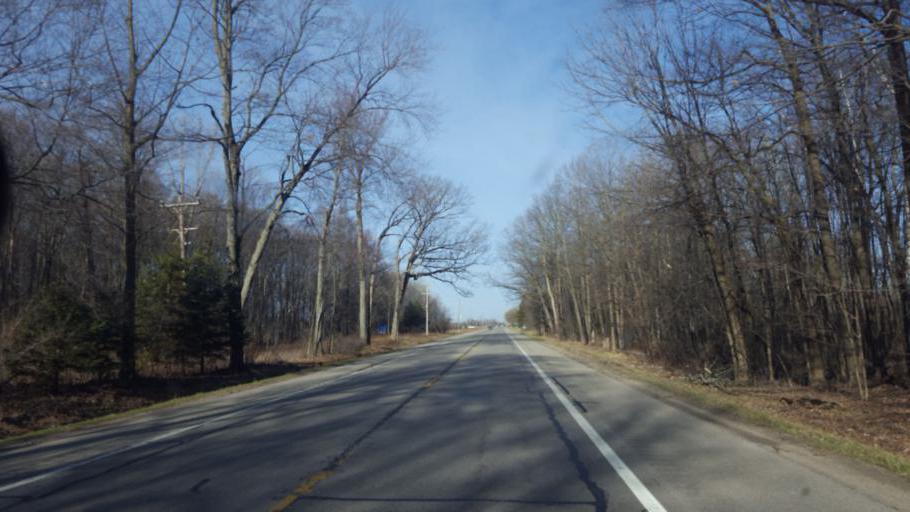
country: US
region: Michigan
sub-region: Montcalm County
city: Edmore
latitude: 43.4080
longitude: -85.0976
